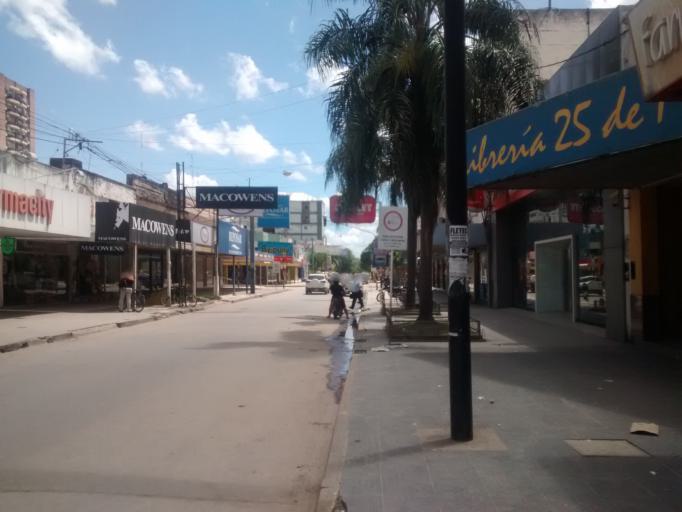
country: AR
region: Chaco
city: Resistencia
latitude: -27.4537
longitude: -58.9860
